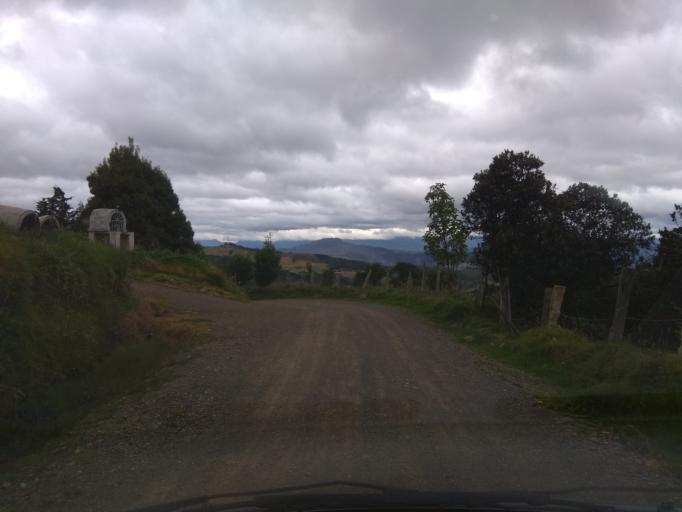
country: CO
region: Boyaca
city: Mongui
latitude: 5.7274
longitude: -72.8400
